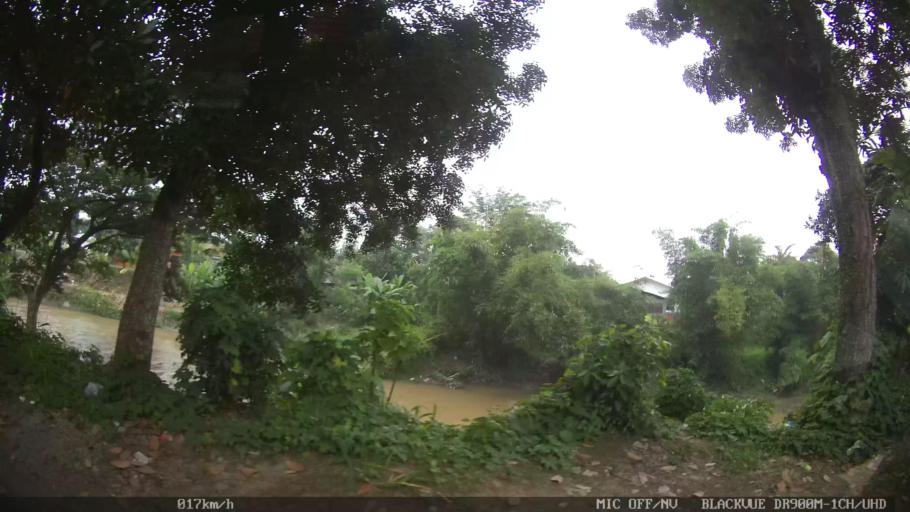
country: ID
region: North Sumatra
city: Deli Tua
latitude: 3.5449
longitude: 98.7158
